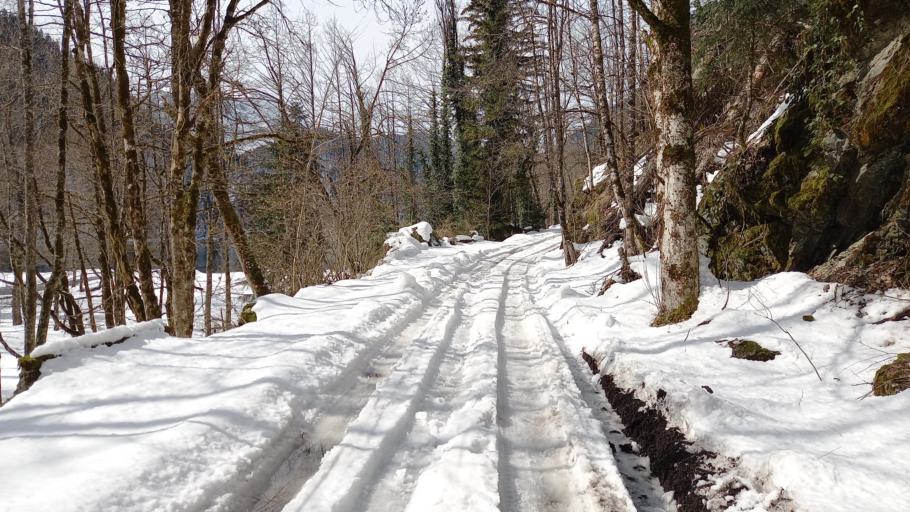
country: GE
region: Abkhazia
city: Gagra
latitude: 43.4823
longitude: 40.5609
